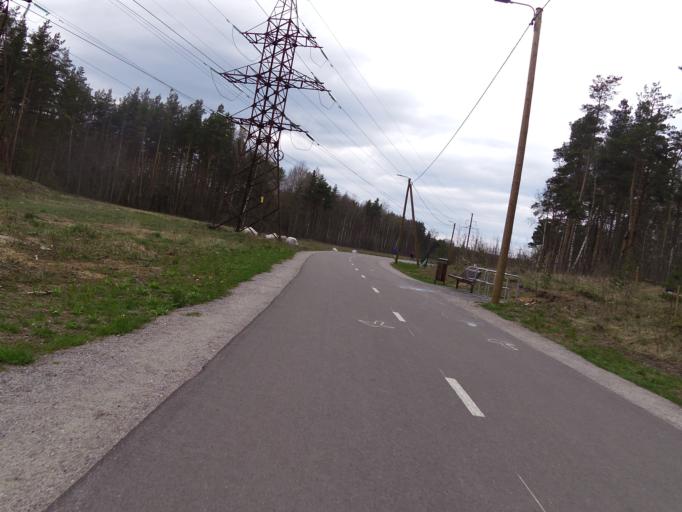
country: EE
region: Harju
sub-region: Tallinna linn
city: Tallinn
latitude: 59.3903
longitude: 24.7342
